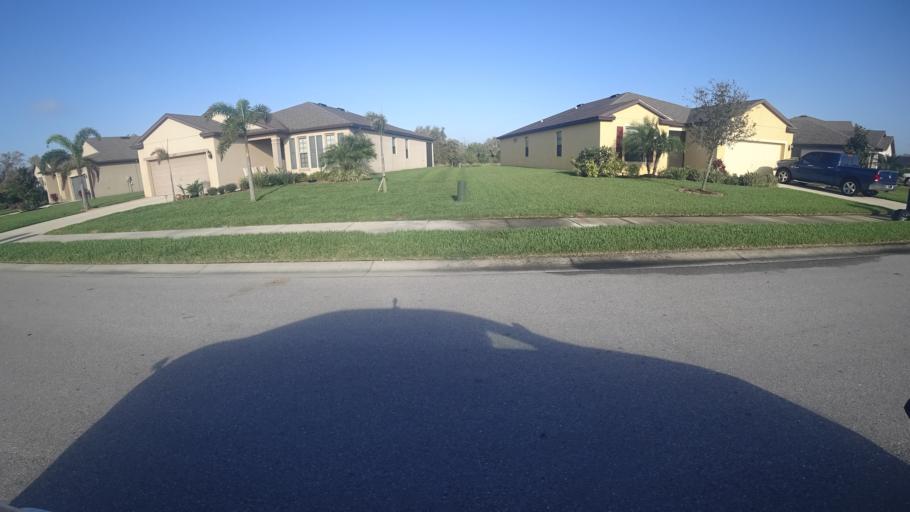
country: US
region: Florida
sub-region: Manatee County
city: Ellenton
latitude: 27.5672
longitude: -82.4511
